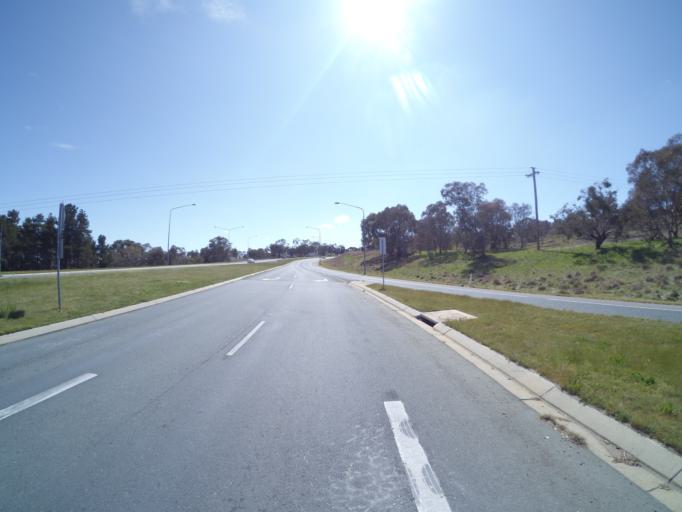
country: AU
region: Australian Capital Territory
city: Macarthur
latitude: -35.4359
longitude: 149.1254
